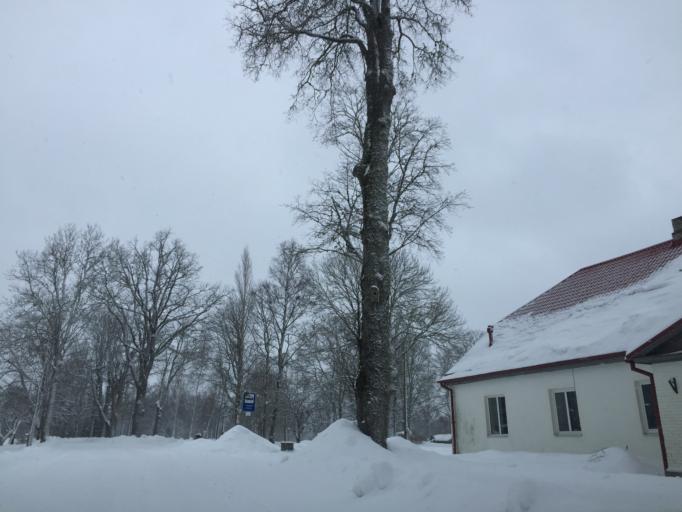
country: LV
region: Amatas Novads
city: Drabesi
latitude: 57.1670
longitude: 25.2783
